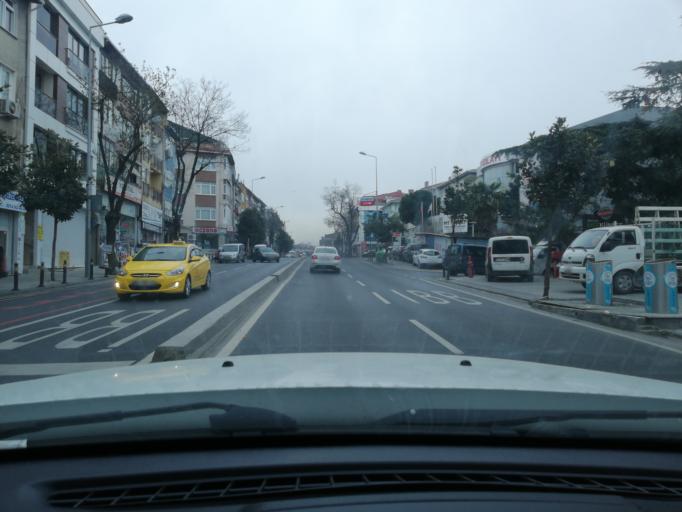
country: TR
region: Istanbul
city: UEskuedar
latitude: 41.0179
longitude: 29.0316
